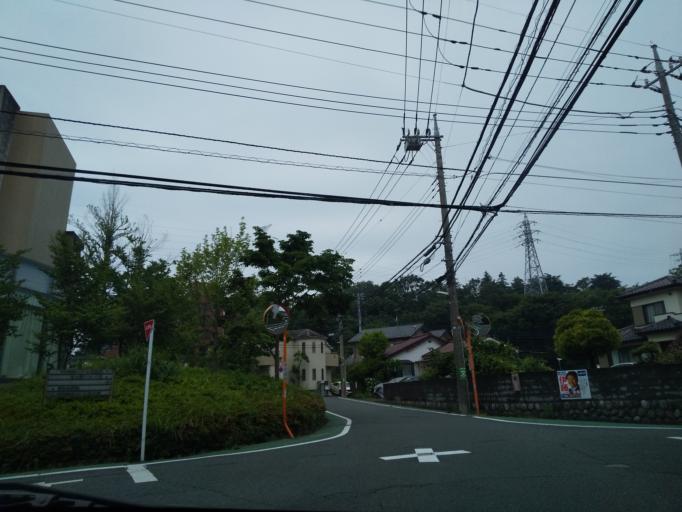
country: JP
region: Tokyo
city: Hino
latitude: 35.6470
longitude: 139.4326
